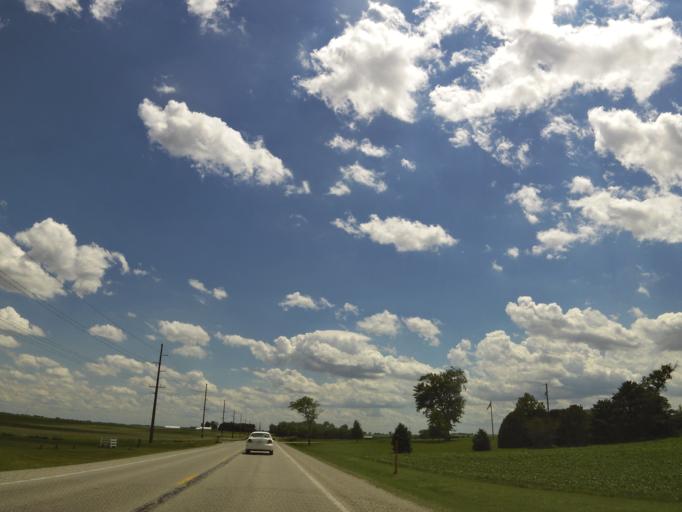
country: US
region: Iowa
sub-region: Buchanan County
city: Independence
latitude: 42.4285
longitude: -91.8897
